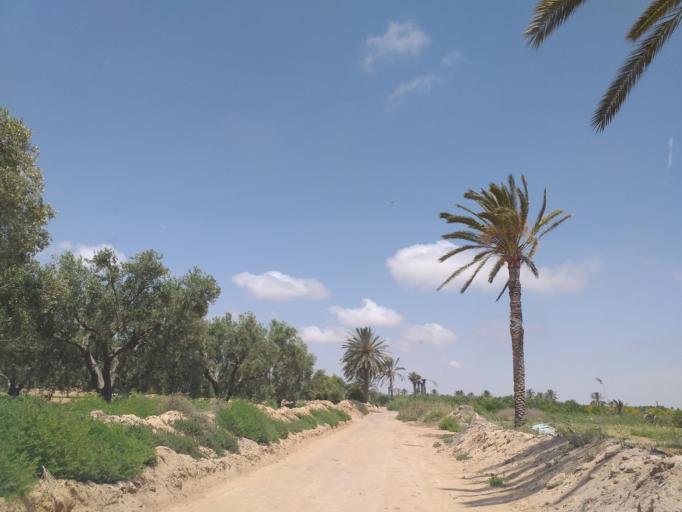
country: TN
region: Qabis
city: Gabes
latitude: 33.9509
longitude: 10.0501
